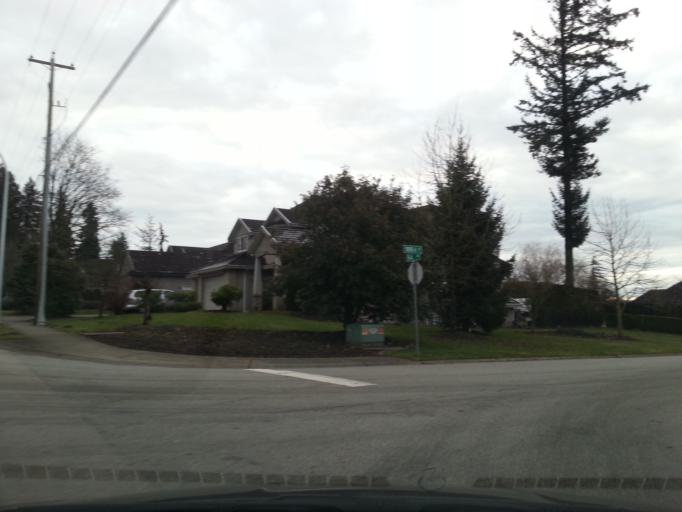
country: CA
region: British Columbia
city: Langley
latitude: 49.1005
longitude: -122.7063
